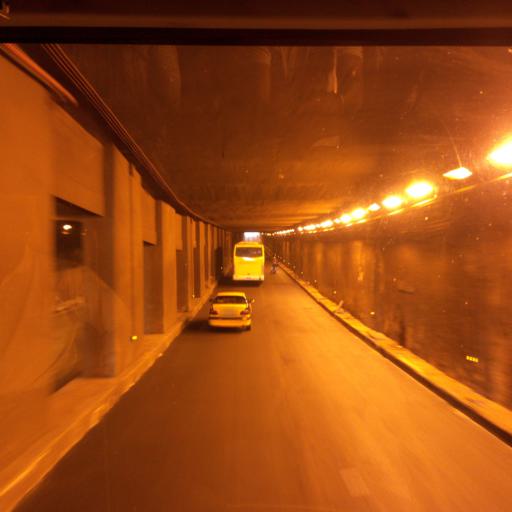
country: SN
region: Dakar
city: Dakar
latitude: 14.6773
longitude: -17.4575
